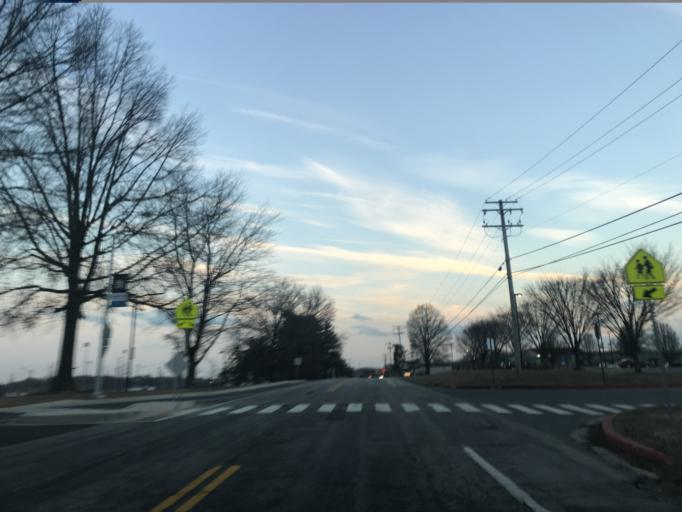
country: US
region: Maryland
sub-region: Harford County
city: South Bel Air
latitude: 39.5594
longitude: -76.2864
